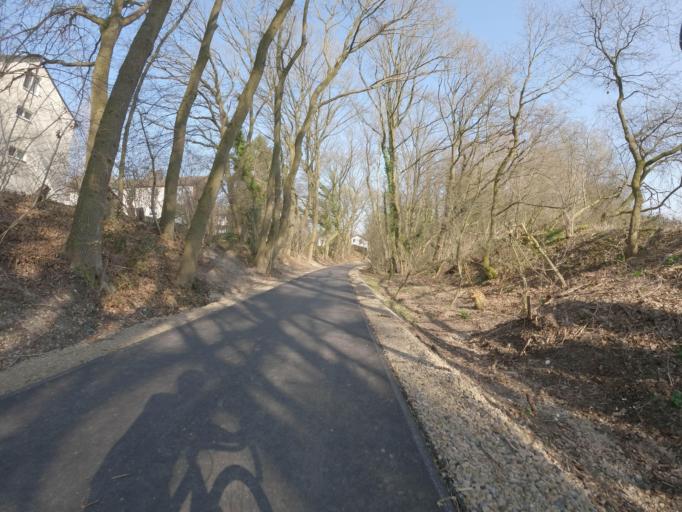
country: DE
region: North Rhine-Westphalia
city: Stolberg
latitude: 50.7790
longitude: 6.1998
